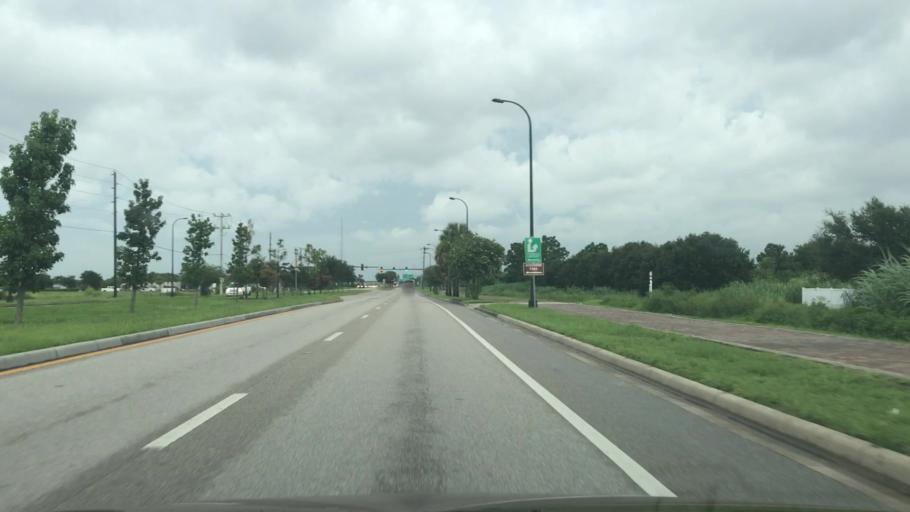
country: US
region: Florida
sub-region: Sarasota County
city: Fruitville
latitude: 27.3386
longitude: -82.4346
